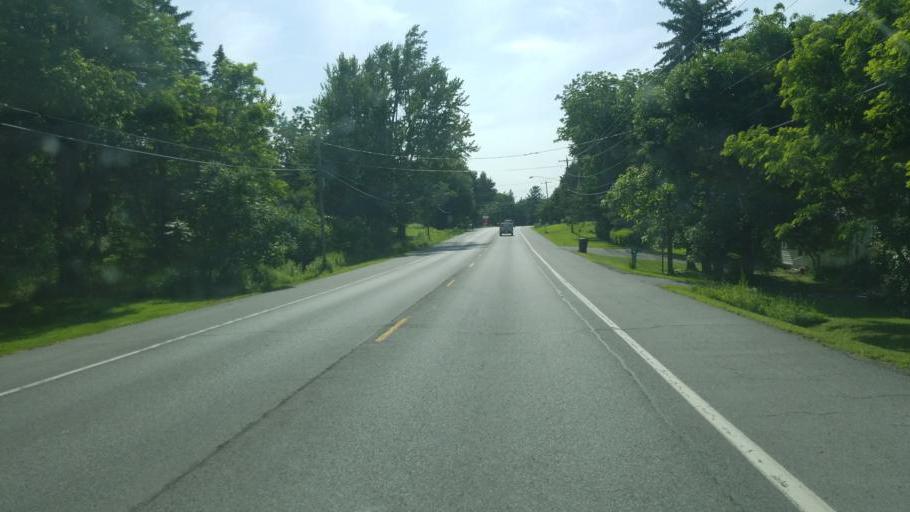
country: US
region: New York
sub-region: Monroe County
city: Honeoye Falls
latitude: 42.9058
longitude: -77.5436
